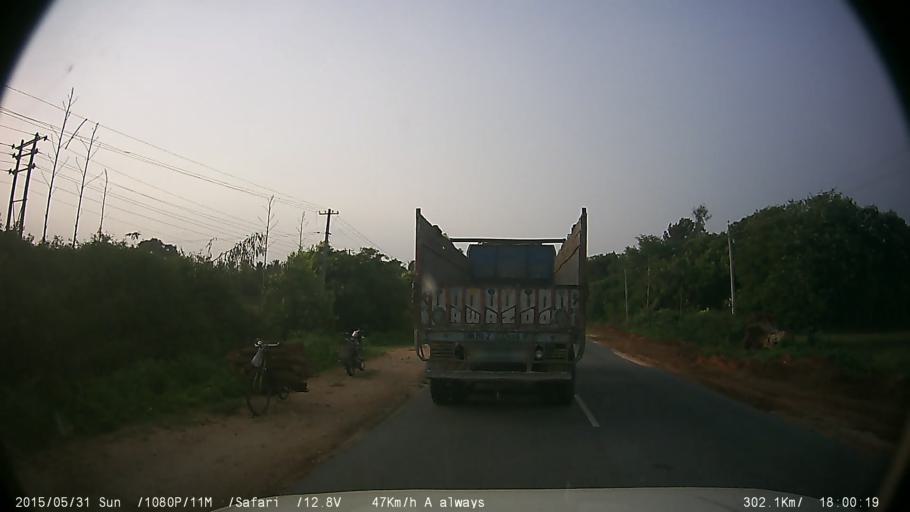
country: IN
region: Karnataka
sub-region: Mysore
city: Nanjangud
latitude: 12.0202
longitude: 76.6728
